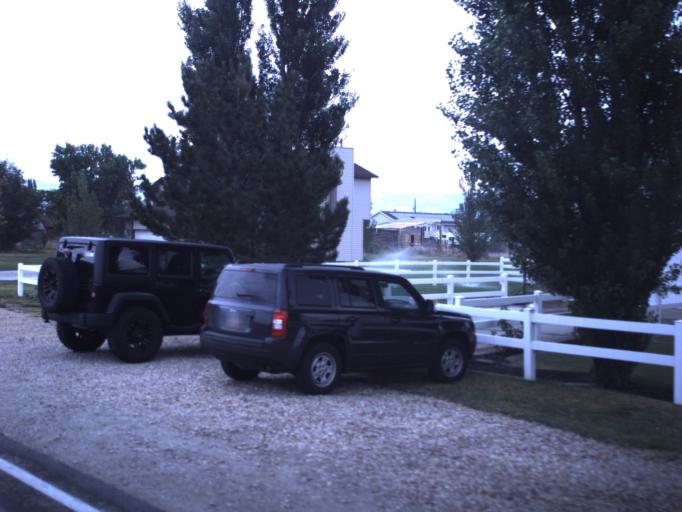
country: US
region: Utah
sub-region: Davis County
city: West Point
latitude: 41.1313
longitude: -112.1126
